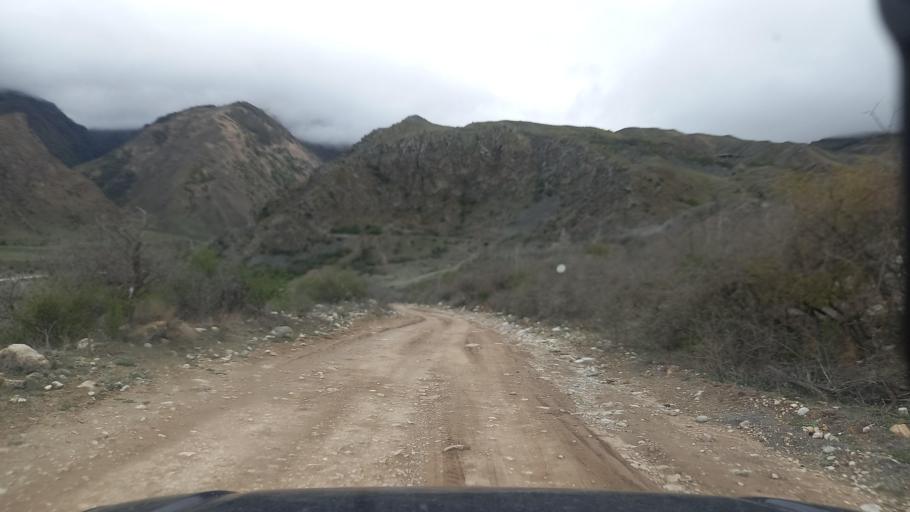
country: RU
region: Kabardino-Balkariya
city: Bylym
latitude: 43.4599
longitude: 43.0099
